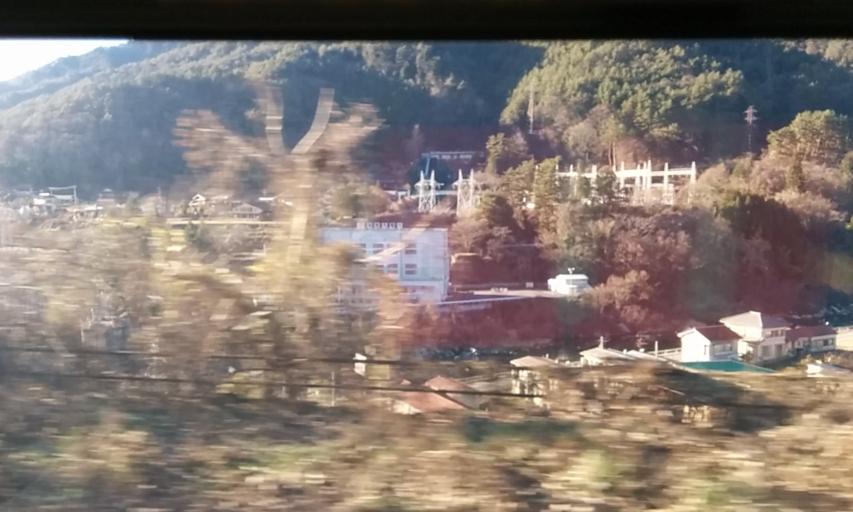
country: JP
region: Nagano
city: Ina
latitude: 35.7799
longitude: 137.6925
